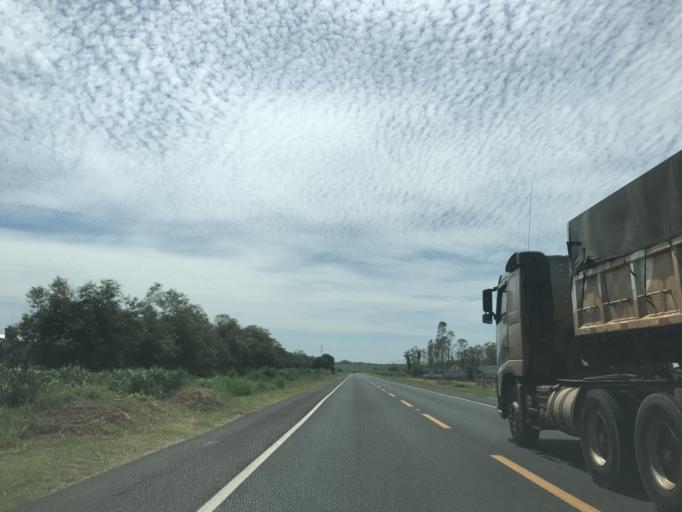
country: BR
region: Parana
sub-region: Paranavai
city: Paranavai
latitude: -23.0148
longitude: -52.5233
